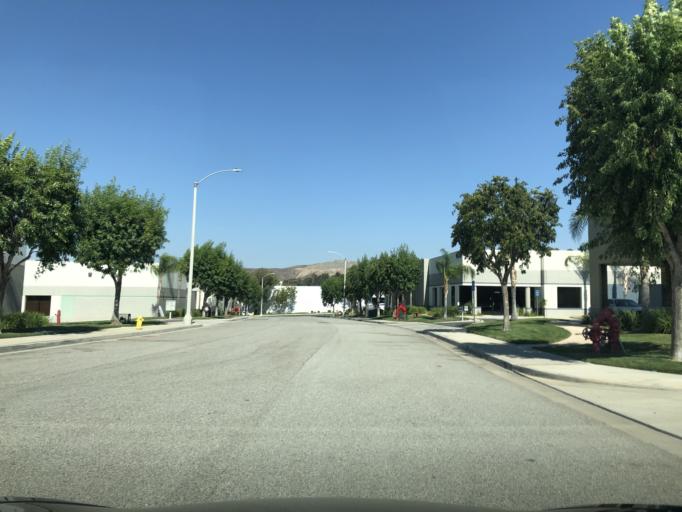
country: US
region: California
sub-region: Riverside County
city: El Cerrito
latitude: 33.8501
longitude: -117.5408
